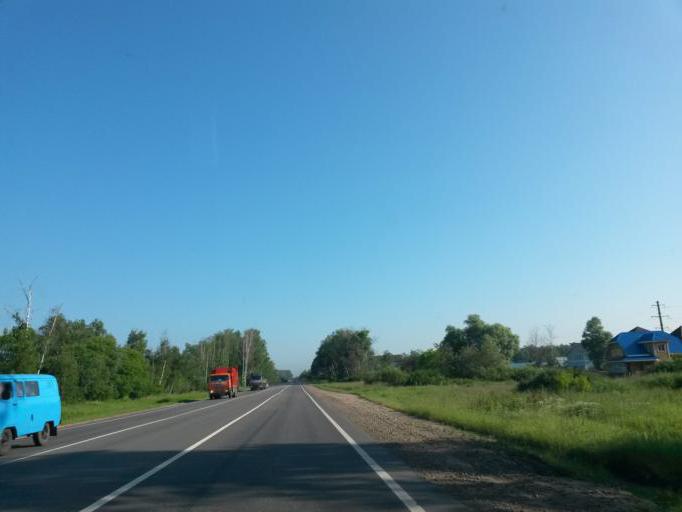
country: RU
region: Moskovskaya
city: Belyye Stolby
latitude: 55.3293
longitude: 37.8053
